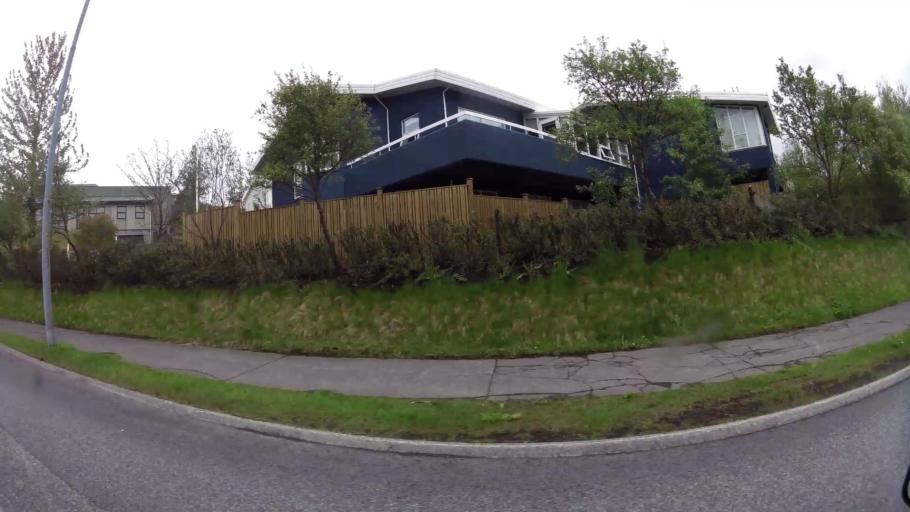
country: IS
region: Capital Region
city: Hafnarfjoerdur
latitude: 64.0596
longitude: -21.9241
